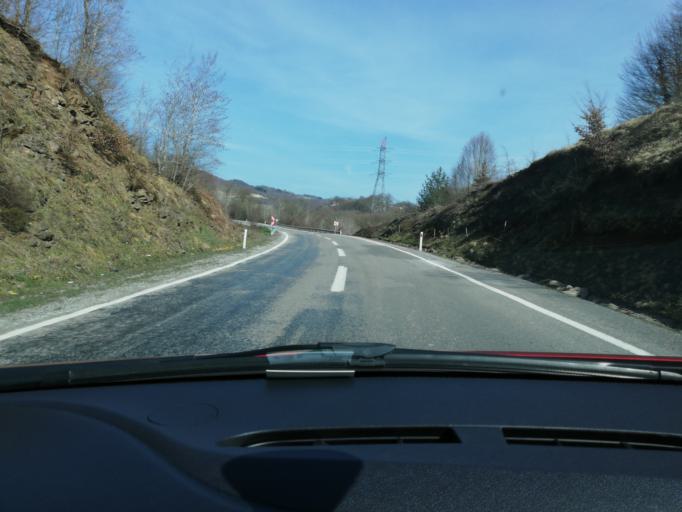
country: TR
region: Bartin
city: Amasra
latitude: 41.7064
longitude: 32.3913
